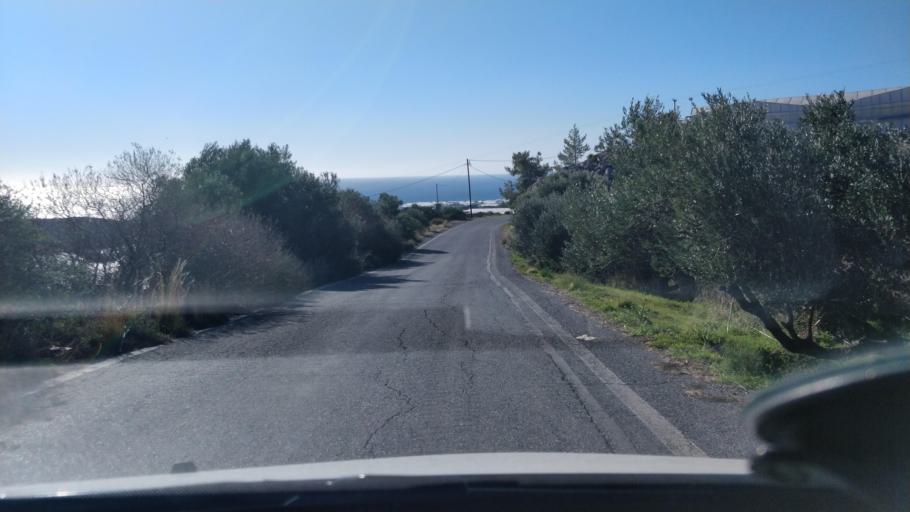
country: GR
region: Crete
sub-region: Nomos Lasithiou
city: Gra Liyia
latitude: 35.0382
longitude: 25.6701
